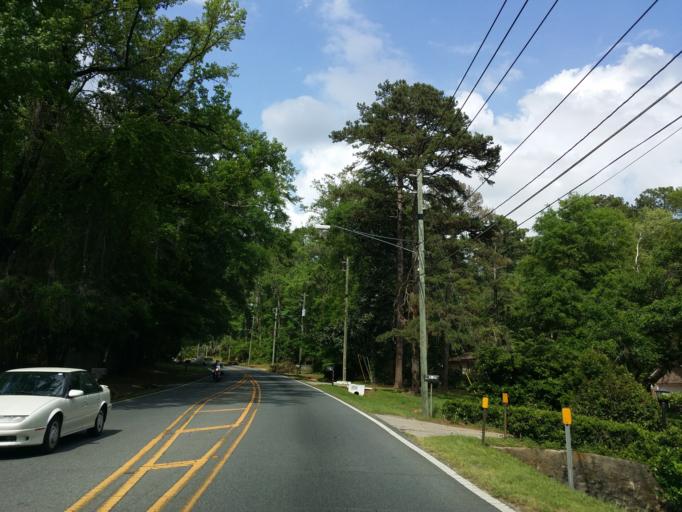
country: US
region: Florida
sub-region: Leon County
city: Tallahassee
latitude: 30.4214
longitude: -84.2636
